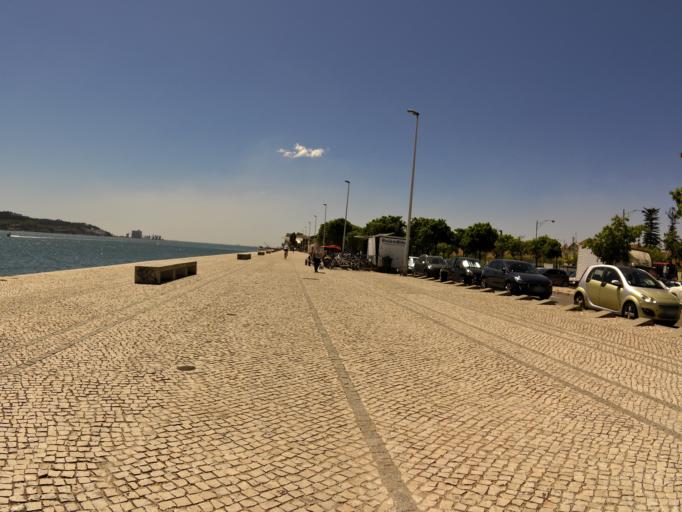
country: PT
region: Setubal
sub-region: Almada
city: Pragal
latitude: 38.6967
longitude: -9.1882
